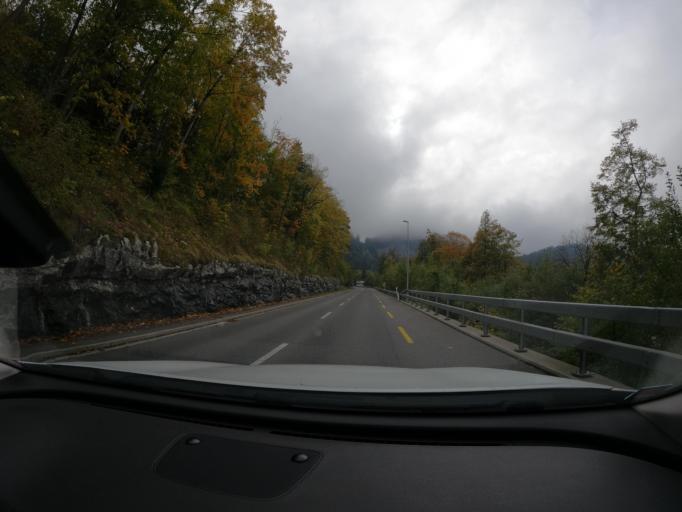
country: CH
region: Obwalden
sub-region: Obwalden
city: Lungern
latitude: 46.7820
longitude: 8.1583
